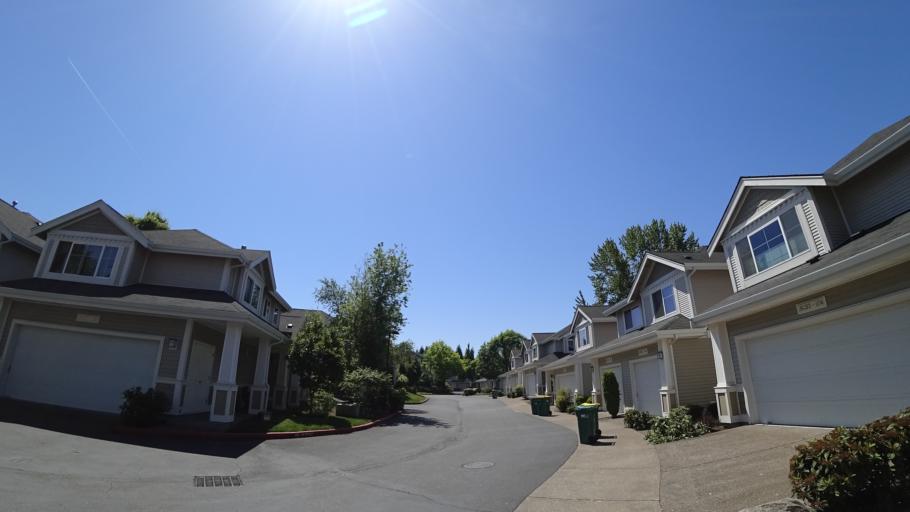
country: US
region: Oregon
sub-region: Washington County
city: Aloha
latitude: 45.4931
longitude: -122.8442
